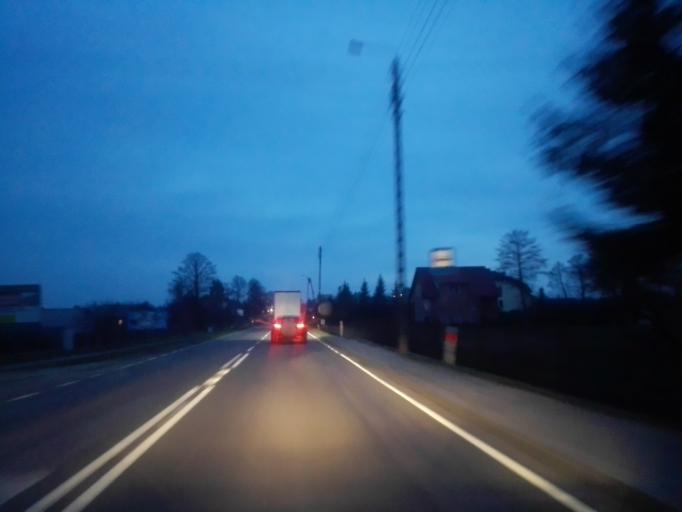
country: PL
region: Podlasie
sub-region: Lomza
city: Lomza
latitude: 53.1274
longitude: 22.0378
